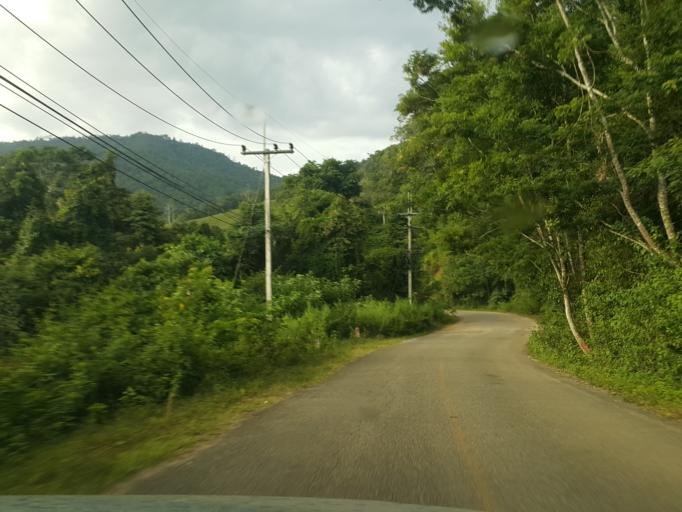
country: TH
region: Mae Hong Son
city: Khun Yuam
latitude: 18.7526
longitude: 98.1923
